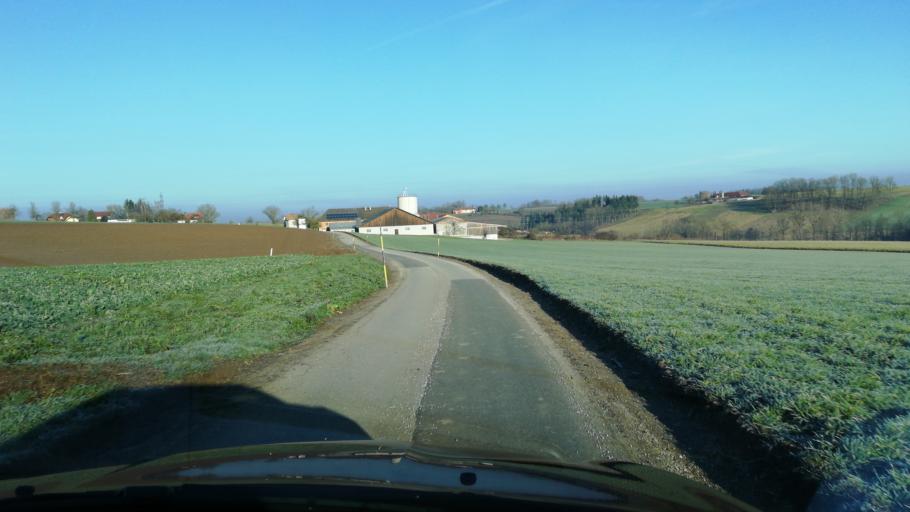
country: AT
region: Upper Austria
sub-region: Politischer Bezirk Steyr-Land
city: Bad Hall
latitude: 48.0475
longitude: 14.2203
